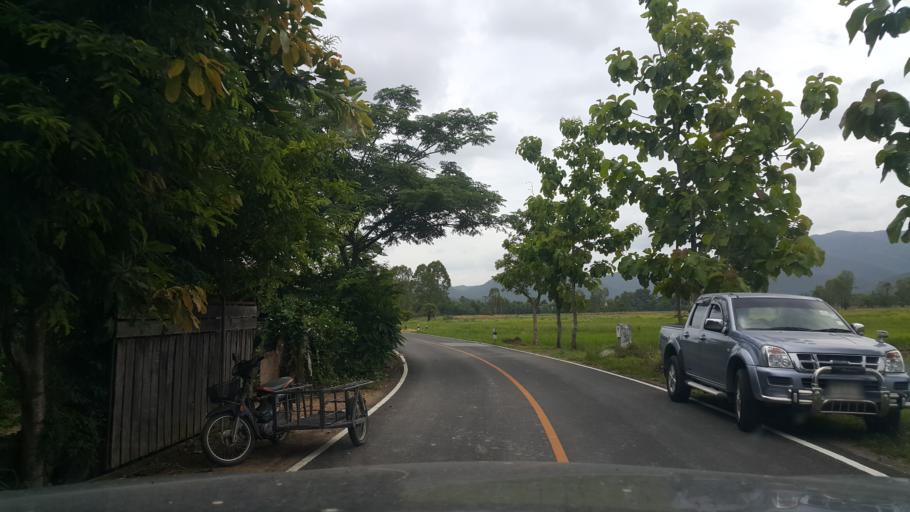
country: TH
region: Lamphun
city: Ban Thi
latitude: 18.6557
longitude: 99.1511
